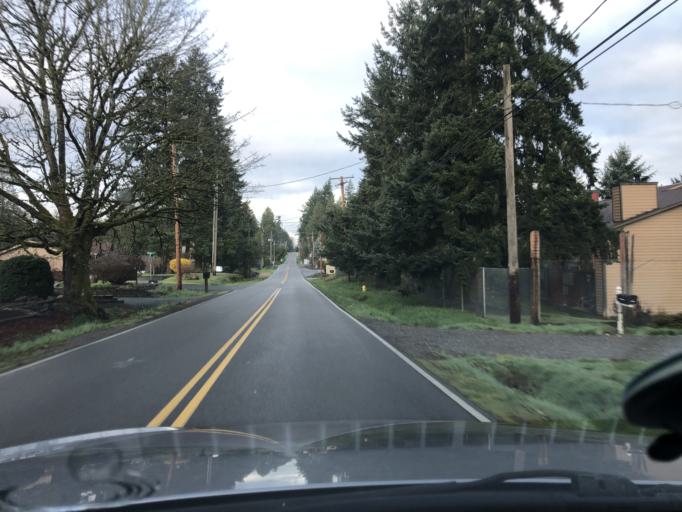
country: US
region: Washington
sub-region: Pierce County
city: Edgewood
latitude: 47.2429
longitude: -122.3018
